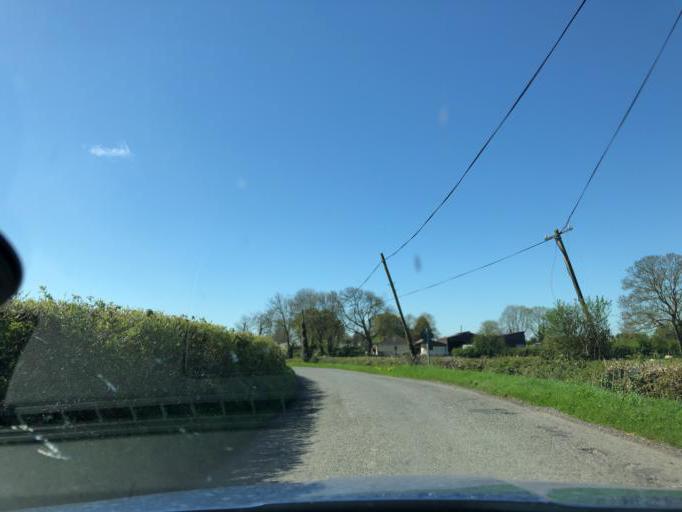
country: IE
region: Connaught
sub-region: County Galway
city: Portumna
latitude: 53.1809
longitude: -8.1760
